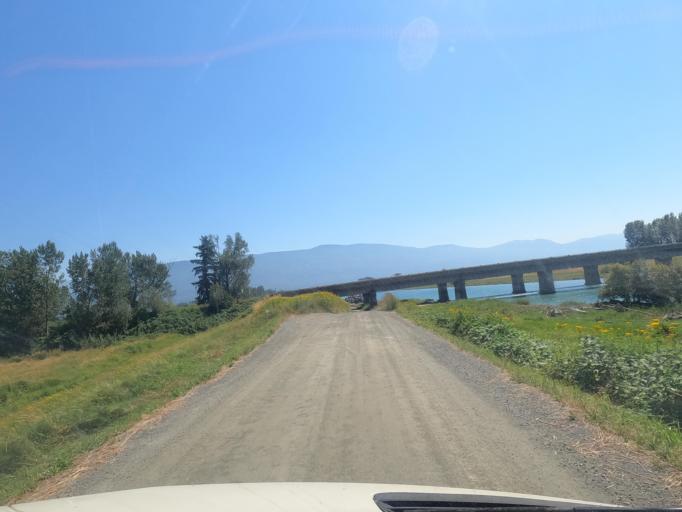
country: CA
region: British Columbia
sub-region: Fraser Valley Regional District
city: Chilliwack
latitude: 49.1245
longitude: -122.0959
